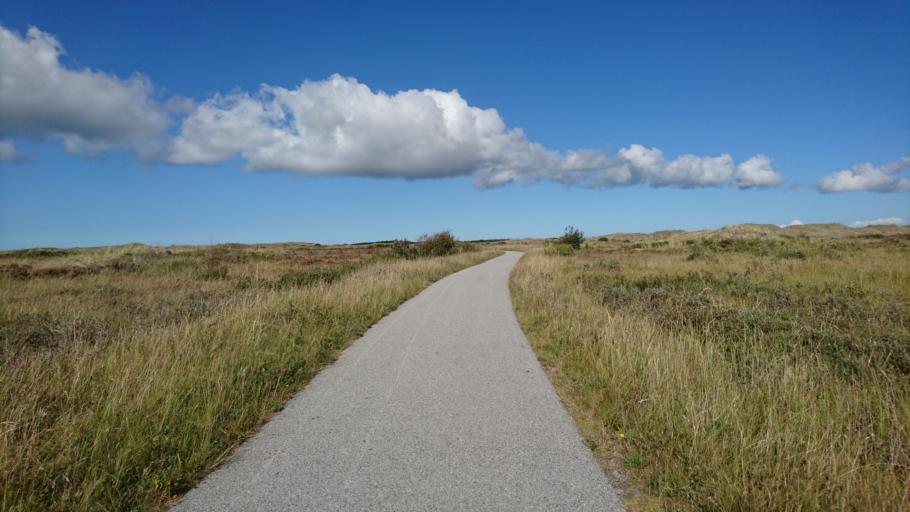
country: DK
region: North Denmark
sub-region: Frederikshavn Kommune
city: Skagen
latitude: 57.6801
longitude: 10.5031
